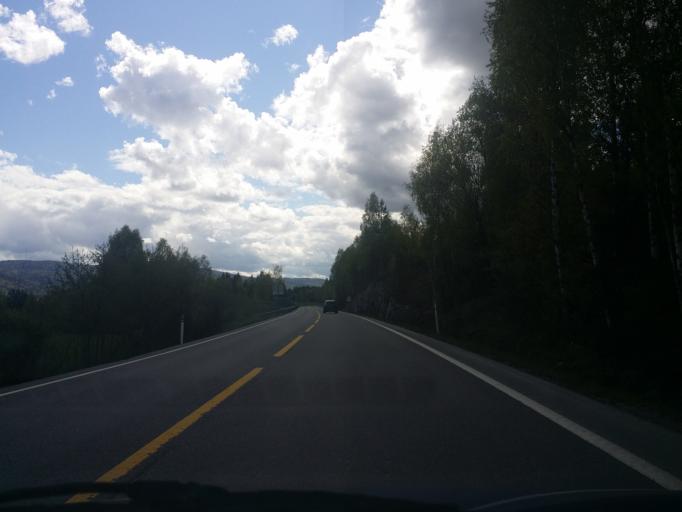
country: NO
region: Buskerud
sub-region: Modum
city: Vikersund
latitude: 59.9627
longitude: 9.9800
